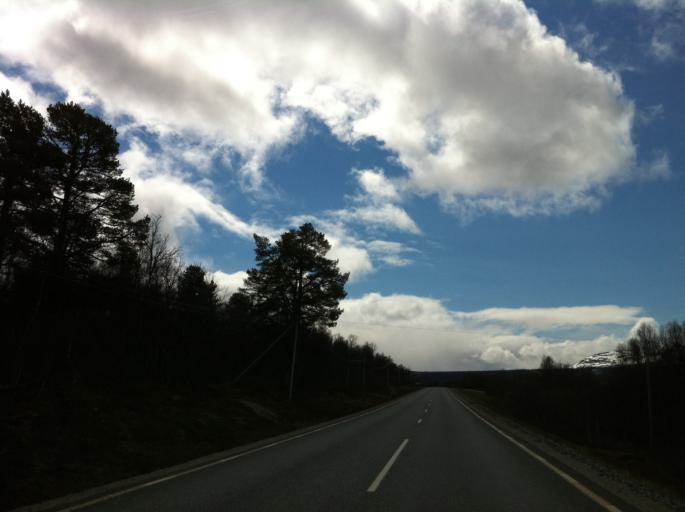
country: NO
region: Sor-Trondelag
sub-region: Tydal
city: Aas
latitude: 62.6546
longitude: 12.4263
